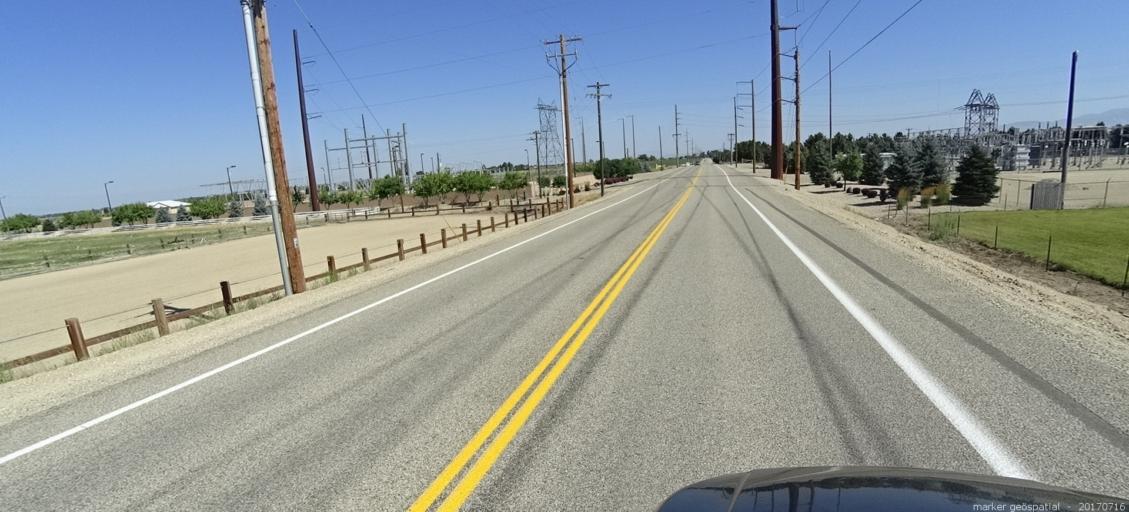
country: US
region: Idaho
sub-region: Ada County
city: Kuna
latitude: 43.5057
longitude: -116.3344
